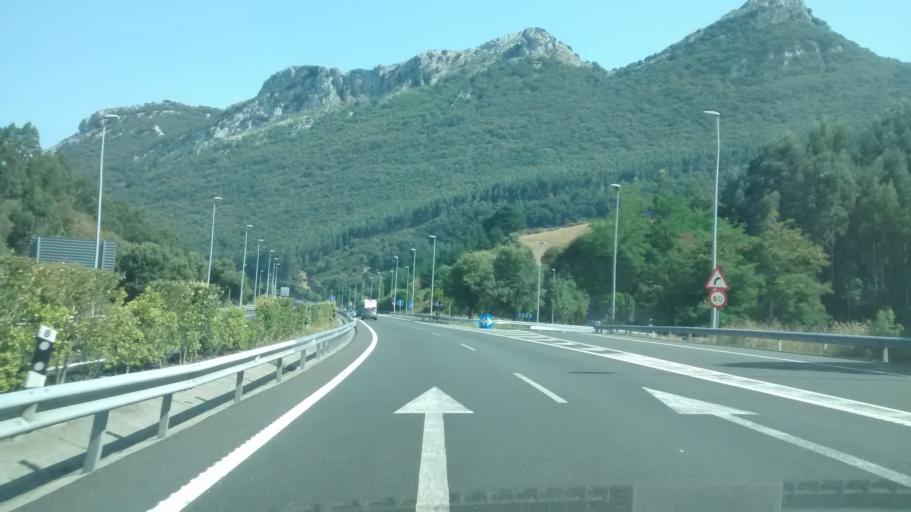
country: ES
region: Cantabria
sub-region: Provincia de Cantabria
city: Liendo
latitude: 43.3863
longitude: -3.3167
